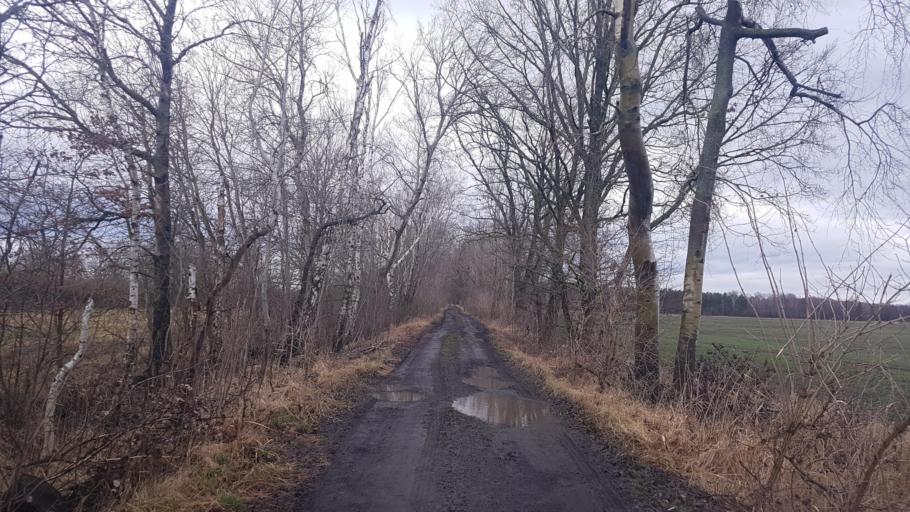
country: DE
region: Brandenburg
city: Grossthiemig
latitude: 51.4296
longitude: 13.6493
